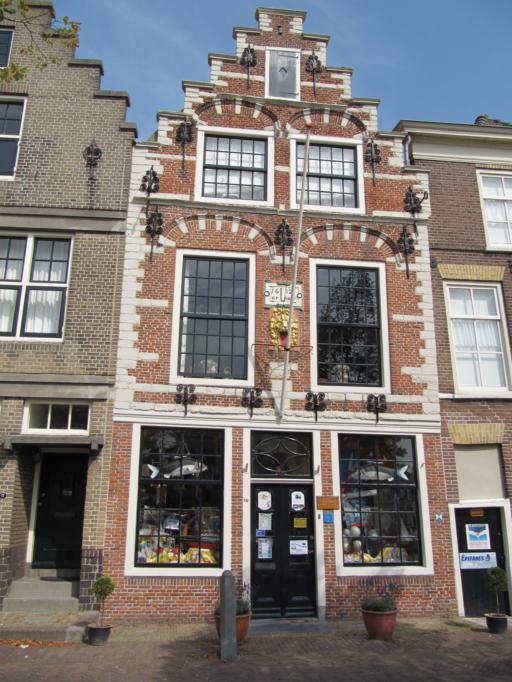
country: NL
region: South Holland
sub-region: Gemeente Brielle
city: Brielle
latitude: 51.9069
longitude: 4.1668
